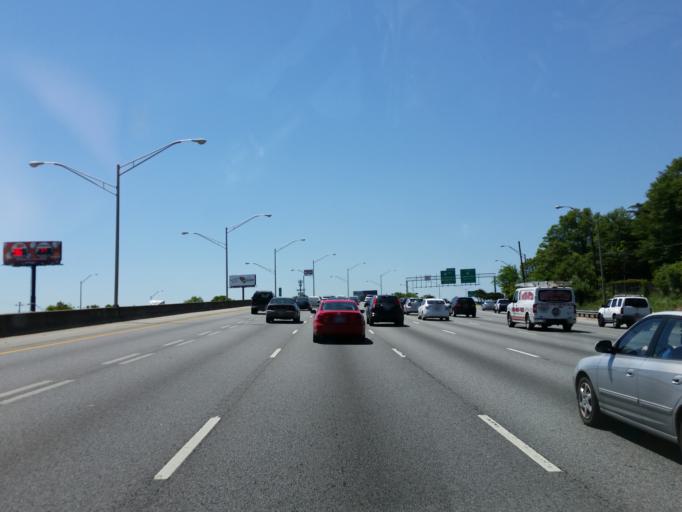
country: US
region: Georgia
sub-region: Fulton County
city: Atlanta
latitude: 33.7250
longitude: -84.3938
